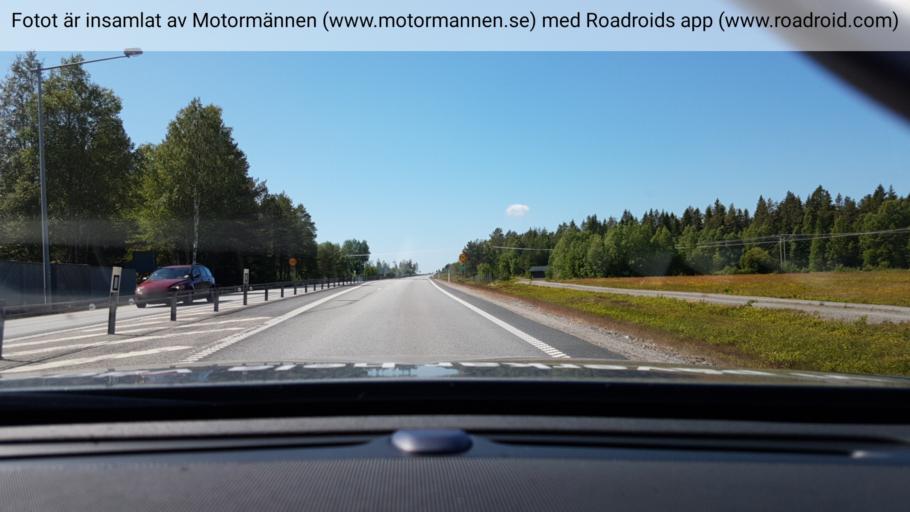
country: SE
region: Vaesterbotten
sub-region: Umea Kommun
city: Hoernefors
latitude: 63.6804
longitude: 19.9982
